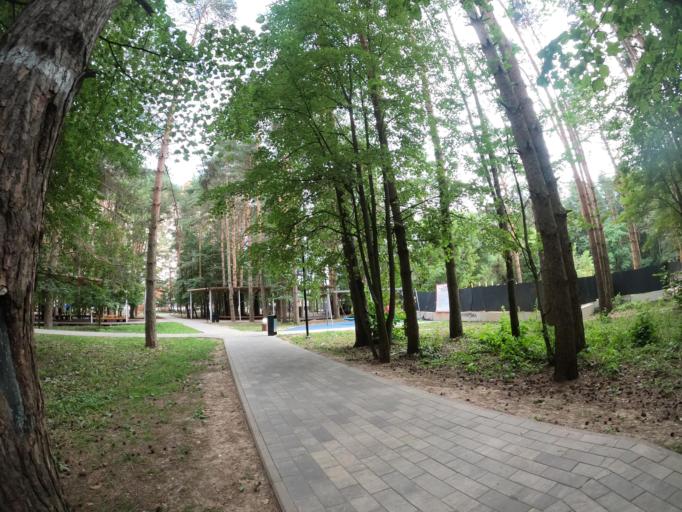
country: RU
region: Moskovskaya
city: Troitsk
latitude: 55.4849
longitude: 37.3022
